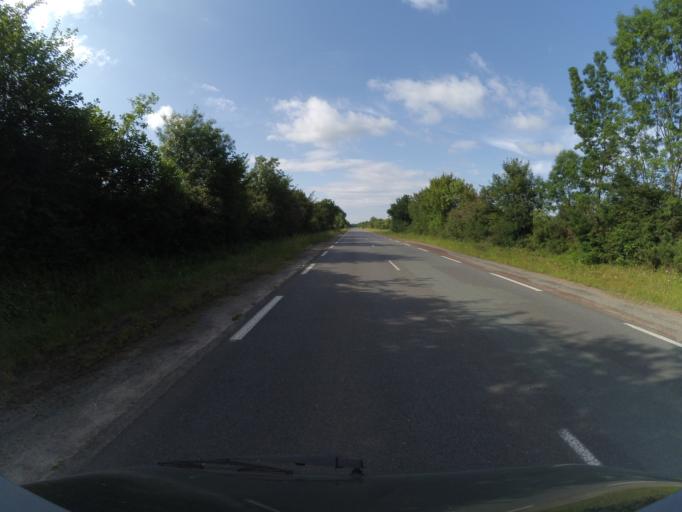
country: FR
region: Poitou-Charentes
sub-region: Departement de la Charente-Maritime
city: Le Gua
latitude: 45.7909
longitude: -0.9361
